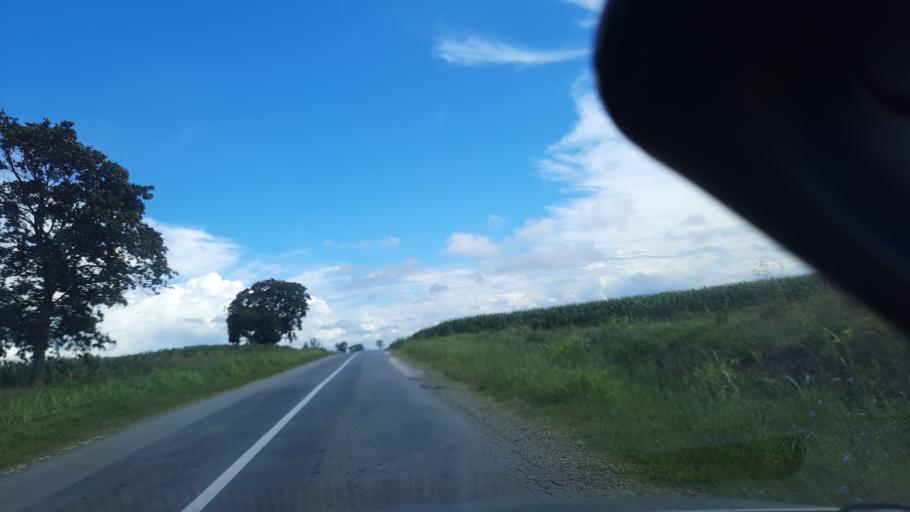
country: RS
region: Autonomna Pokrajina Vojvodina
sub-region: Sremski Okrug
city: Sremska Mitrovica
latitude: 45.0933
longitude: 19.5737
